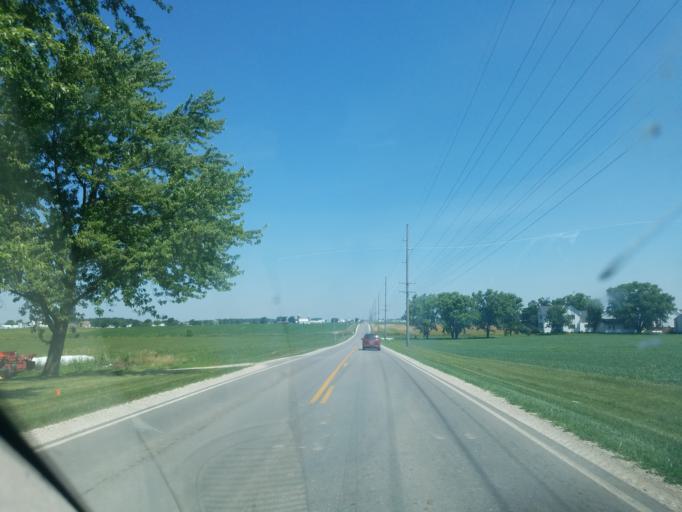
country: US
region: Ohio
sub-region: Mercer County
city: Saint Henry
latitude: 40.4409
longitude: -84.6481
